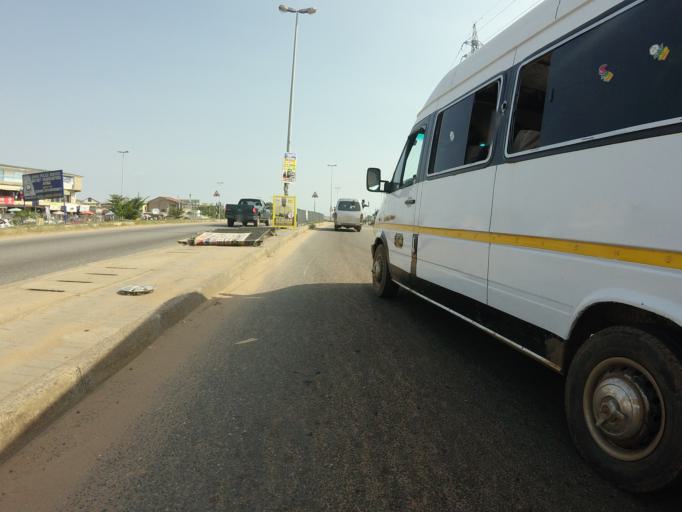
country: GH
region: Greater Accra
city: Gbawe
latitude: 5.5989
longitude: -0.2910
